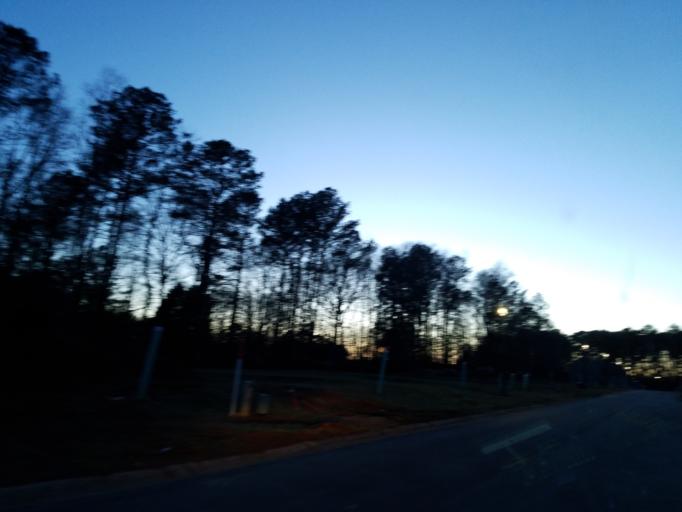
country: US
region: Georgia
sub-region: Cherokee County
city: Holly Springs
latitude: 34.1687
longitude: -84.4097
